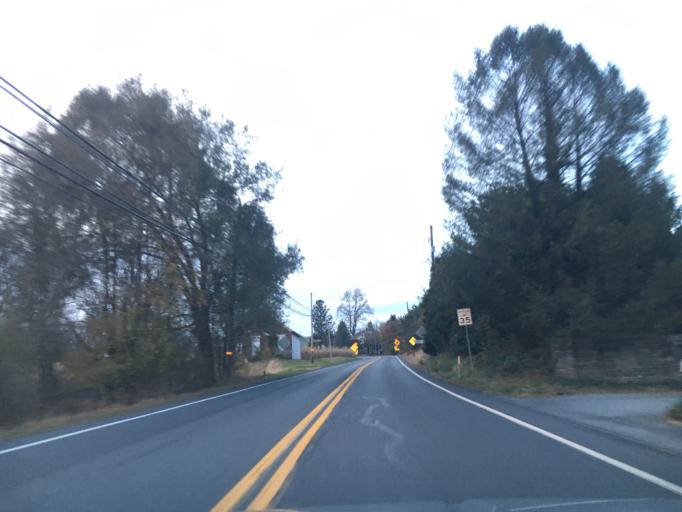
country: US
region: Pennsylvania
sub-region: Lehigh County
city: Stiles
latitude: 40.6486
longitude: -75.5344
